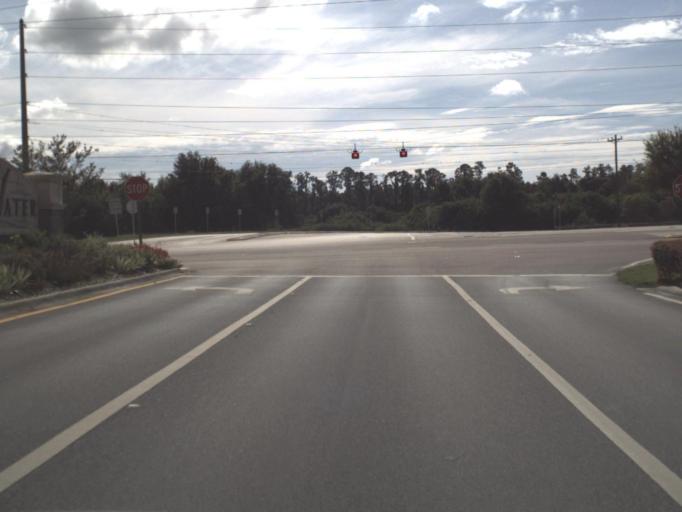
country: US
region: Florida
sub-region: Polk County
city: Combee Settlement
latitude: 28.1180
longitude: -81.9087
